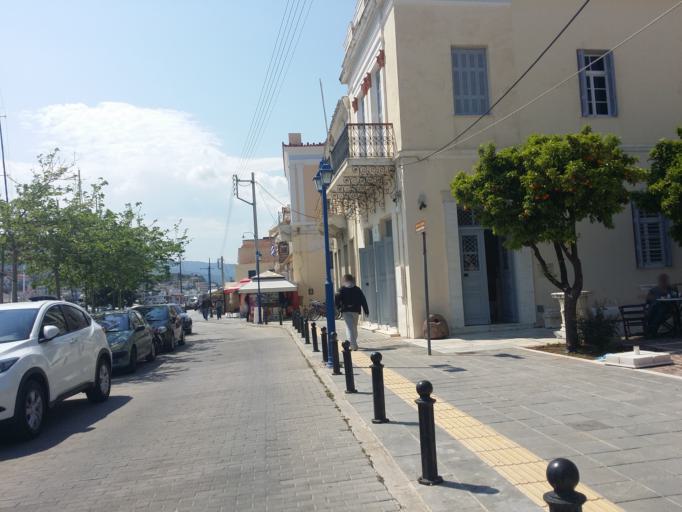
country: GR
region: Attica
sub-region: Nomos Piraios
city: Poros
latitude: 37.4983
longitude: 23.4548
